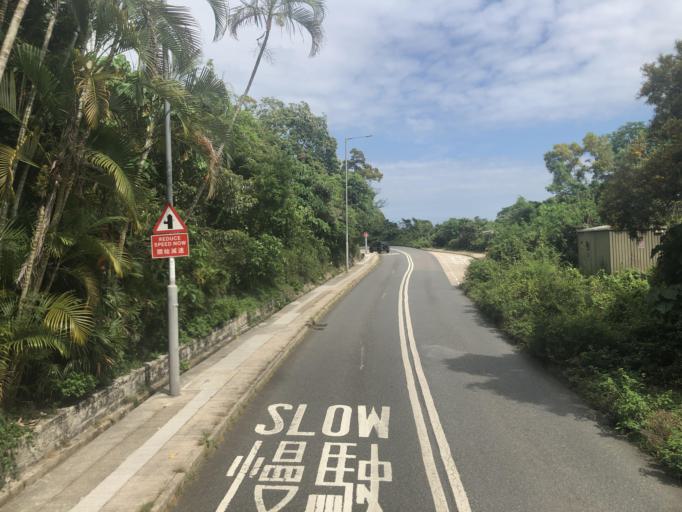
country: HK
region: Sai Kung
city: Sai Kung
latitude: 22.3892
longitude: 114.2923
